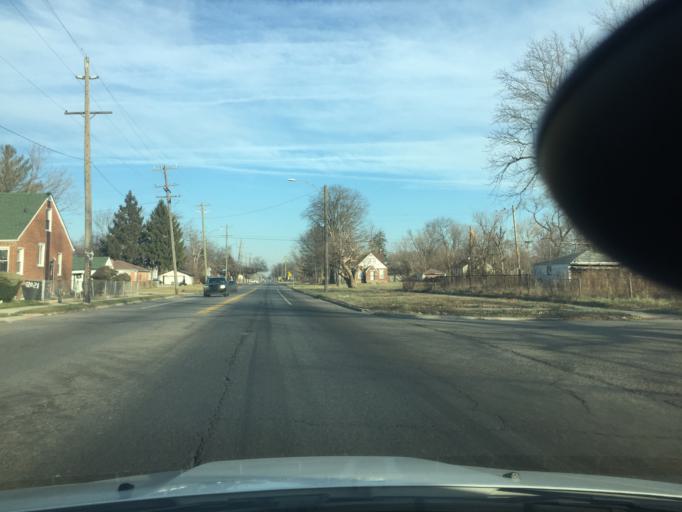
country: US
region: Michigan
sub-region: Macomb County
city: Eastpointe
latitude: 42.4371
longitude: -82.9655
